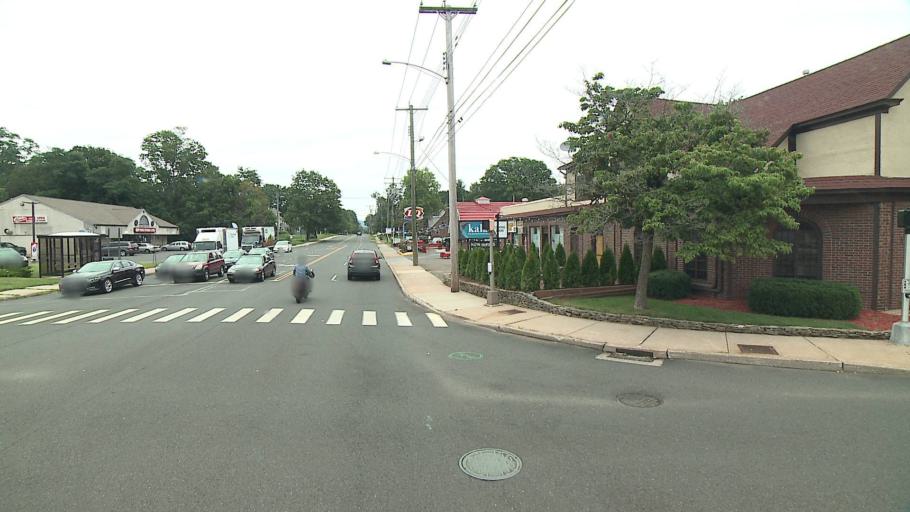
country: US
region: Connecticut
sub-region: New Haven County
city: Hamden
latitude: 41.3711
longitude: -72.9062
